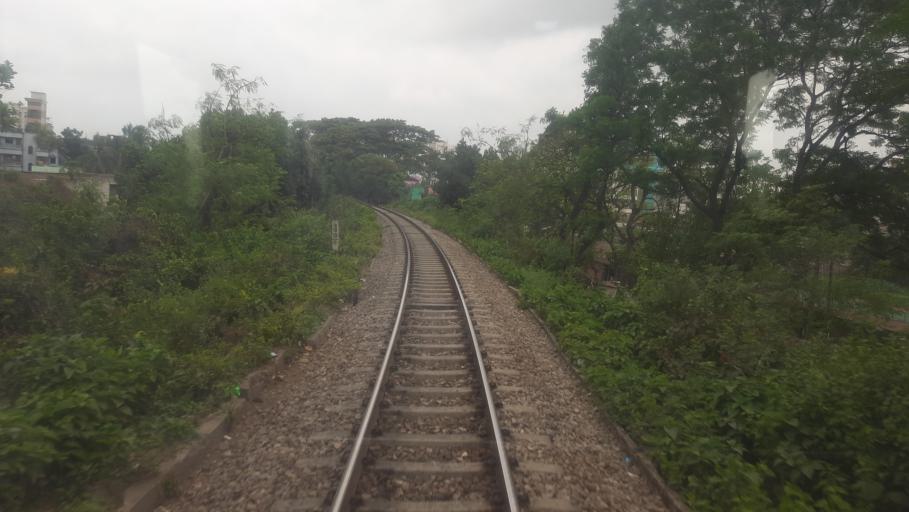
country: BD
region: Dhaka
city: Bhairab Bazar
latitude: 24.0505
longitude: 90.9882
